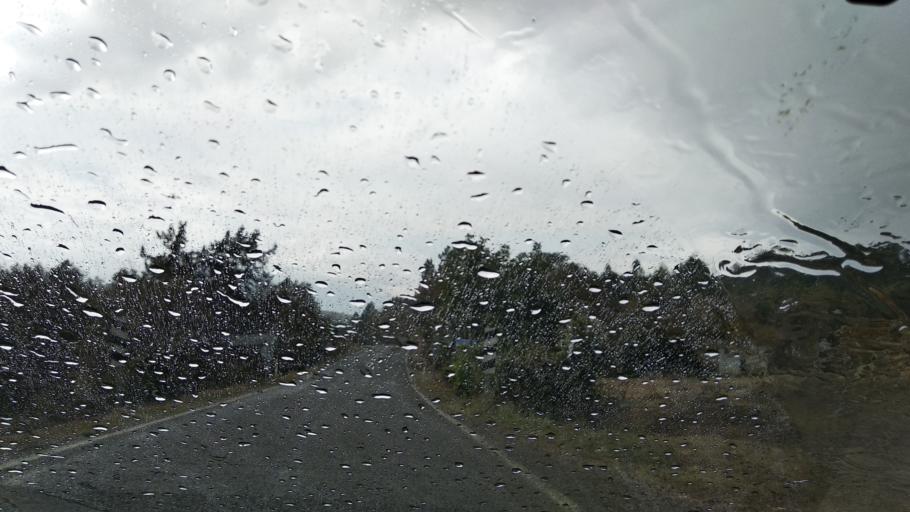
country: TR
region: Ankara
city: Nallihan
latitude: 40.3283
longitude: 31.4096
